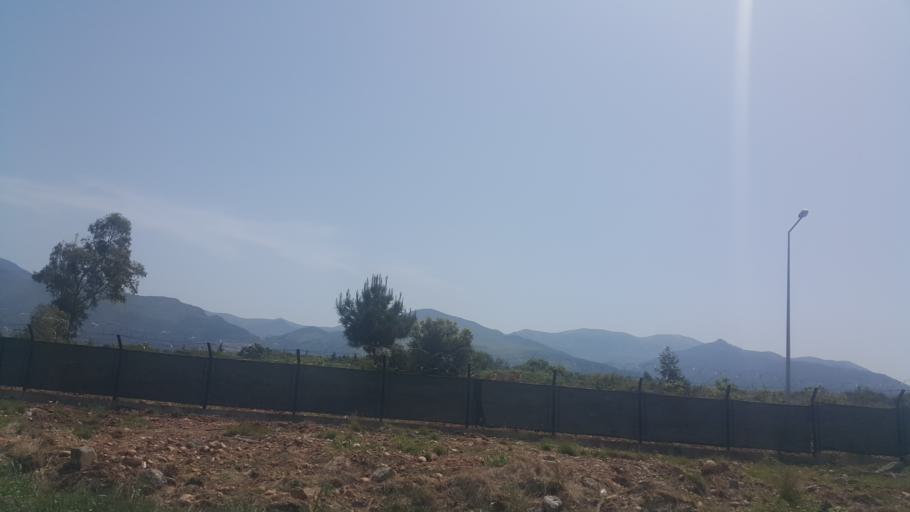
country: TR
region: Hatay
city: Denizciler
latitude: 36.6304
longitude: 36.1999
